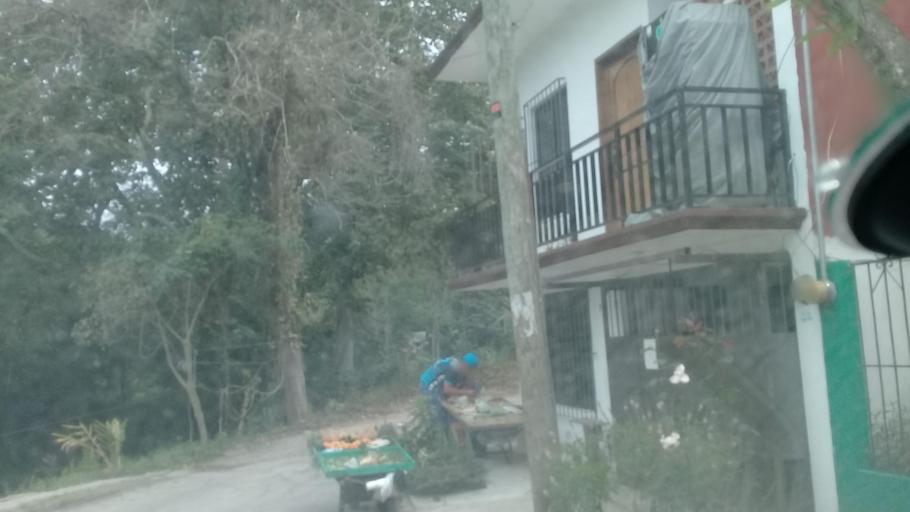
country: MX
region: Veracruz
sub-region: Xalapa
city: Xalapa de Enriquez
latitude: 19.5189
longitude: -96.9053
